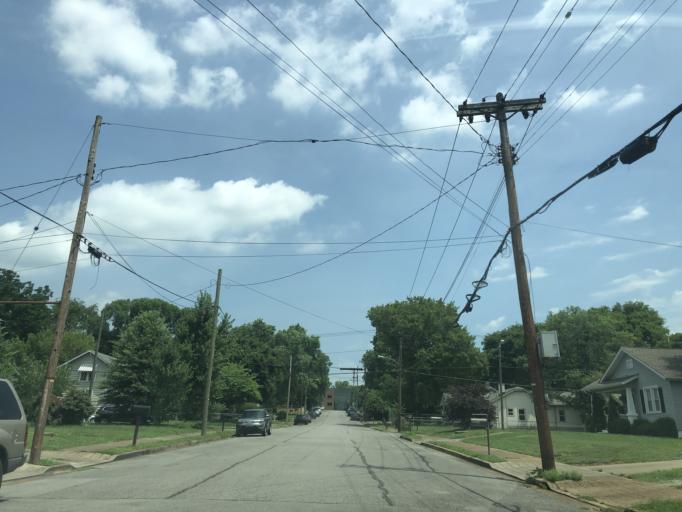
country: US
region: Tennessee
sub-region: Davidson County
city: Nashville
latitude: 36.1917
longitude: -86.7688
